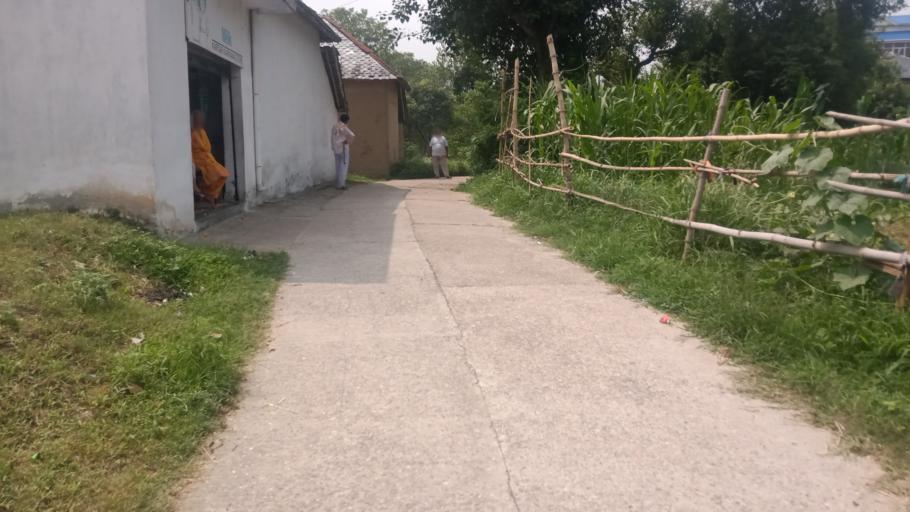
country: IN
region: Himachal Pradesh
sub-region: Hamirpur
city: Nadaun
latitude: 31.6933
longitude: 76.3573
